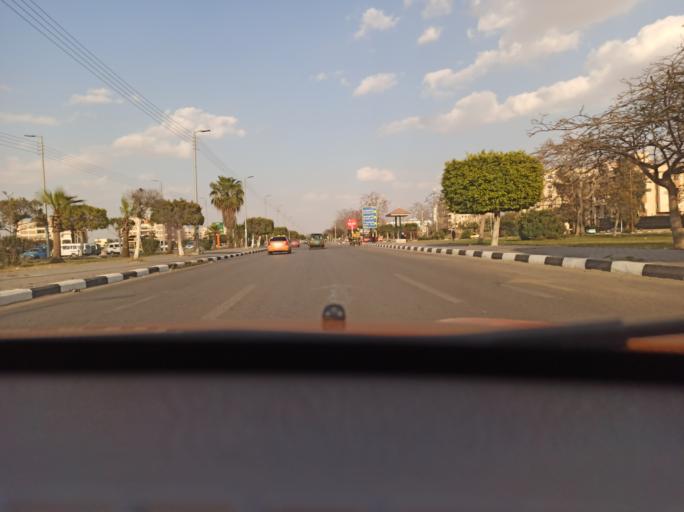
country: EG
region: Al Isma'iliyah
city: Ismailia
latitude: 30.6202
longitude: 32.2809
